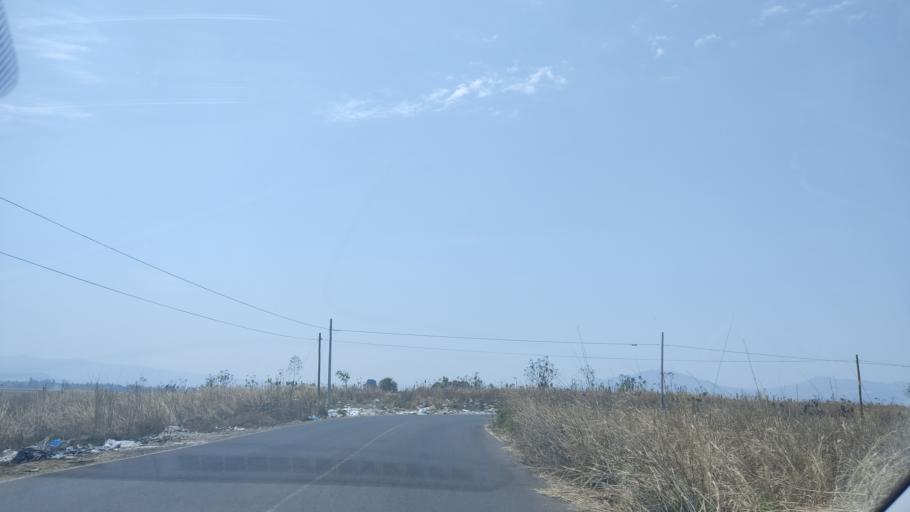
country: MX
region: Nayarit
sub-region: Tepic
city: La Corregidora
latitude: 21.4882
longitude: -104.8050
